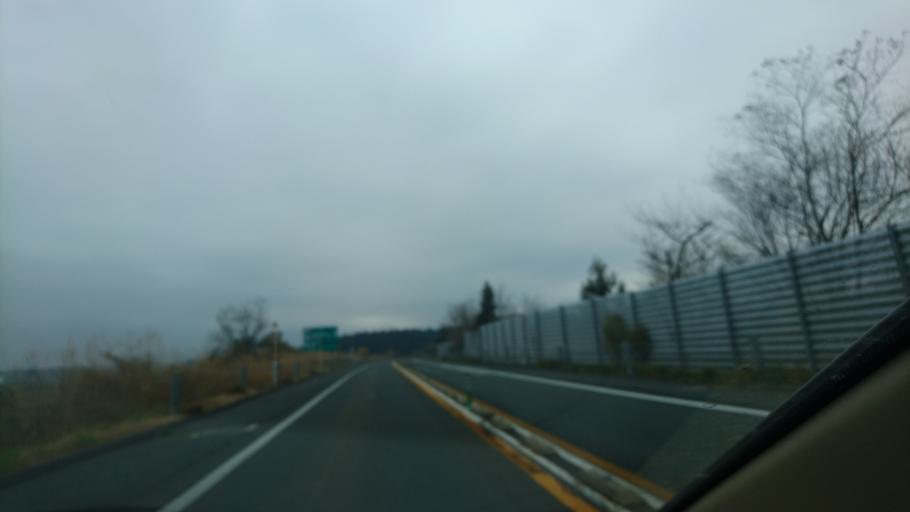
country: JP
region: Iwate
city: Kitakami
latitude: 39.2780
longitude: 141.0559
